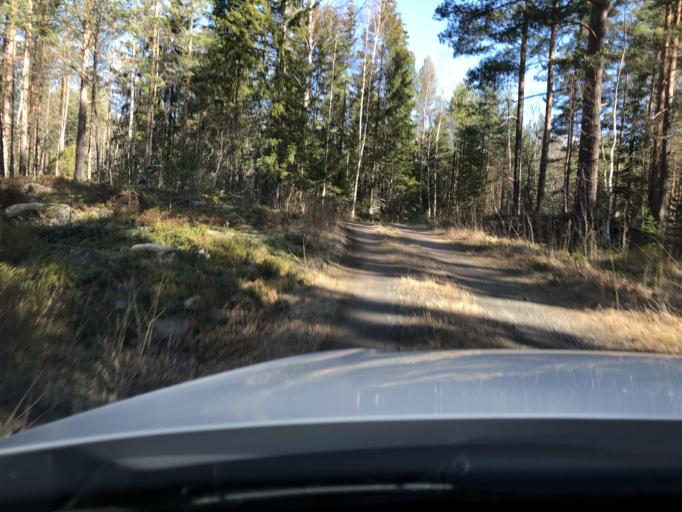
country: SE
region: Uppsala
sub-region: Heby Kommun
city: OEstervala
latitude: 60.3285
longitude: 17.1741
